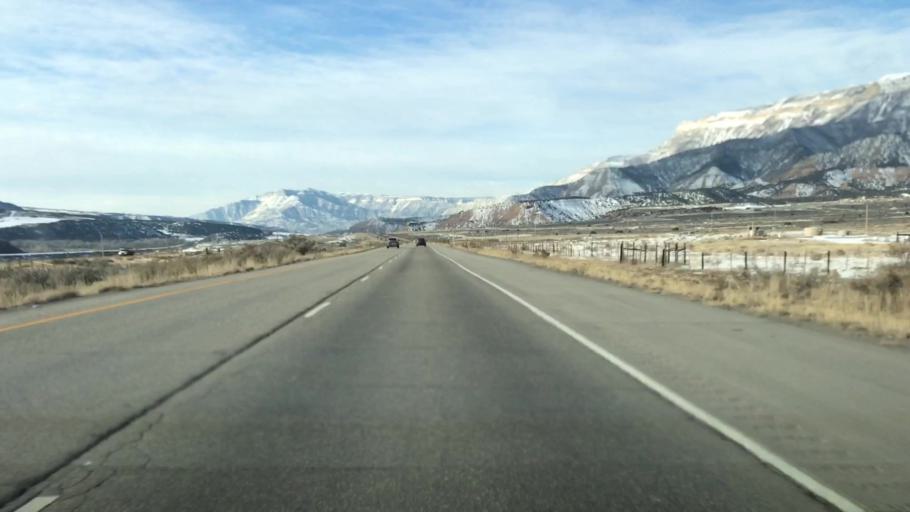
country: US
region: Colorado
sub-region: Garfield County
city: Rifle
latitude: 39.5060
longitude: -107.8904
